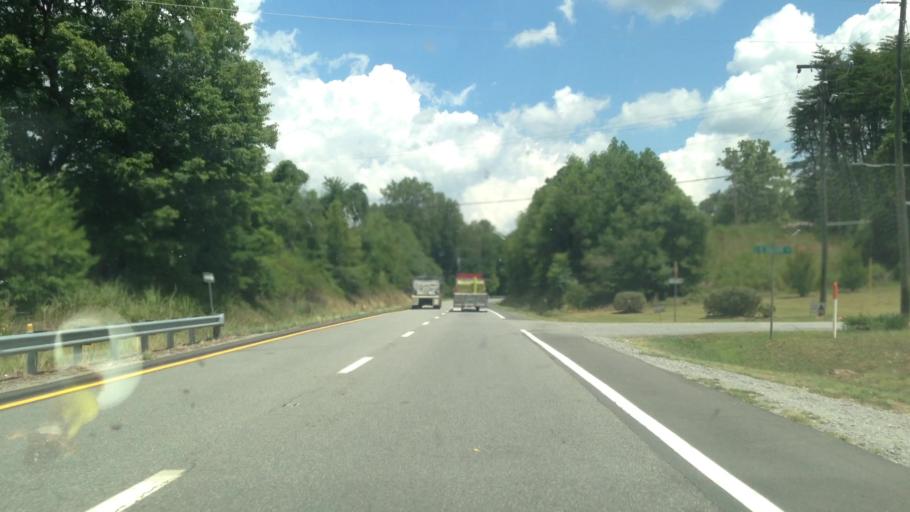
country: US
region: North Carolina
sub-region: Rockingham County
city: Stoneville
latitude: 36.5548
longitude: -79.8907
